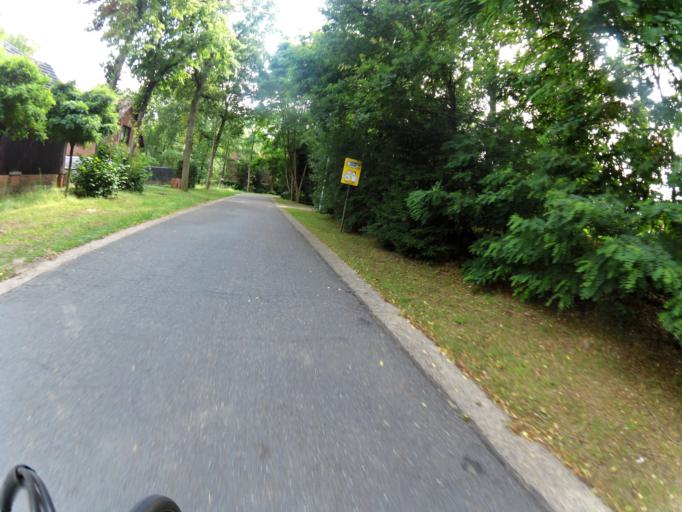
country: BE
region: Flanders
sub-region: Provincie Antwerpen
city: Balen
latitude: 51.1909
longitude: 5.1996
